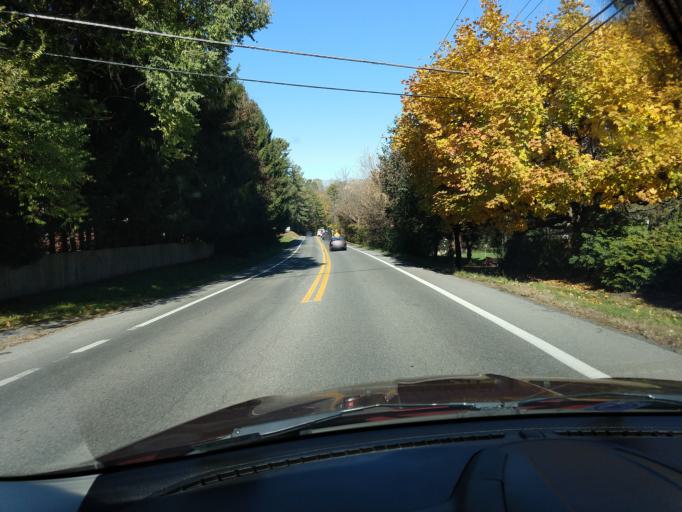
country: US
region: West Virginia
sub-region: Greenbrier County
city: Lewisburg
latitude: 37.7963
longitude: -80.4472
